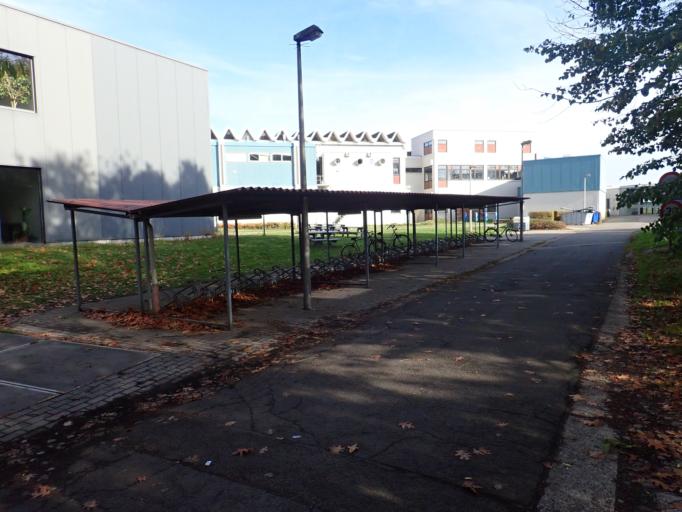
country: BE
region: Flanders
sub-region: Provincie Antwerpen
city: Duffel
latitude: 51.0674
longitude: 4.4987
